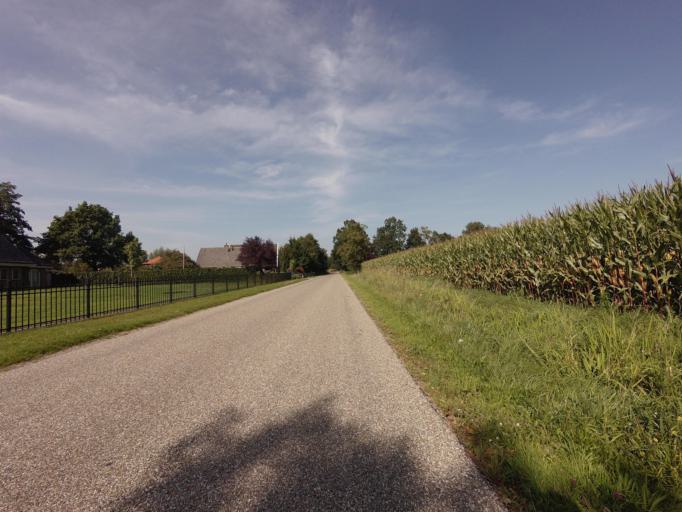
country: NL
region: Overijssel
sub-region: Gemeente Hof van Twente
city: Hengevelde
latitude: 52.2465
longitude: 6.6346
